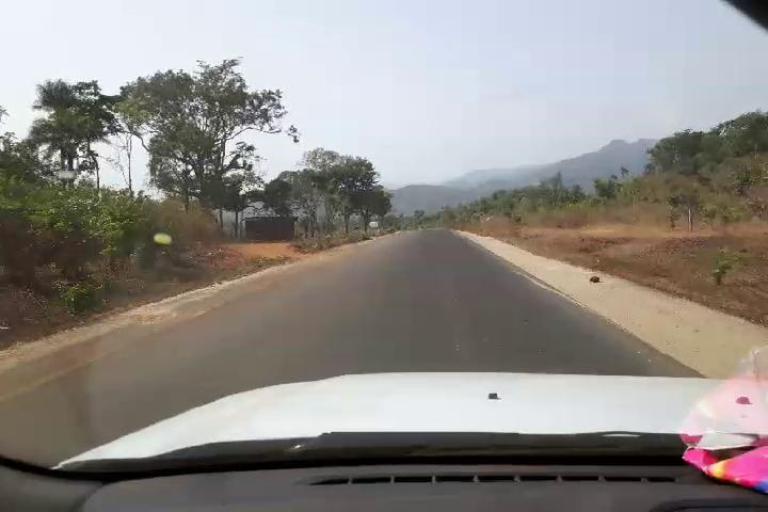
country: SL
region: Western Area
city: Waterloo
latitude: 8.2669
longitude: -13.1604
